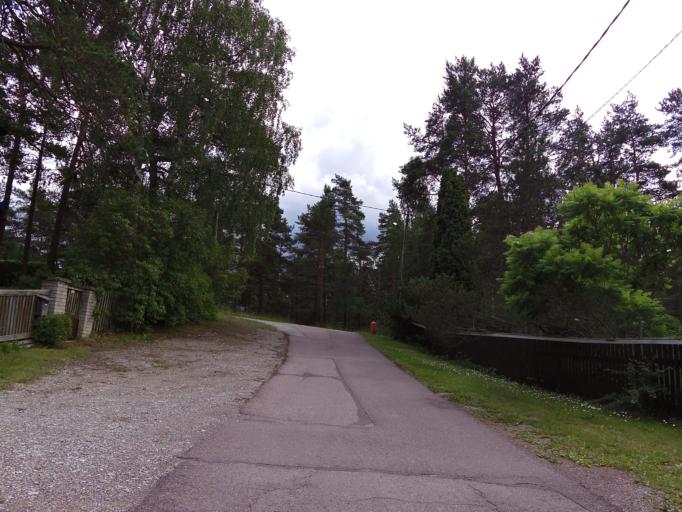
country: EE
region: Harju
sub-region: Saue vald
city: Laagri
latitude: 59.3866
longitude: 24.6573
